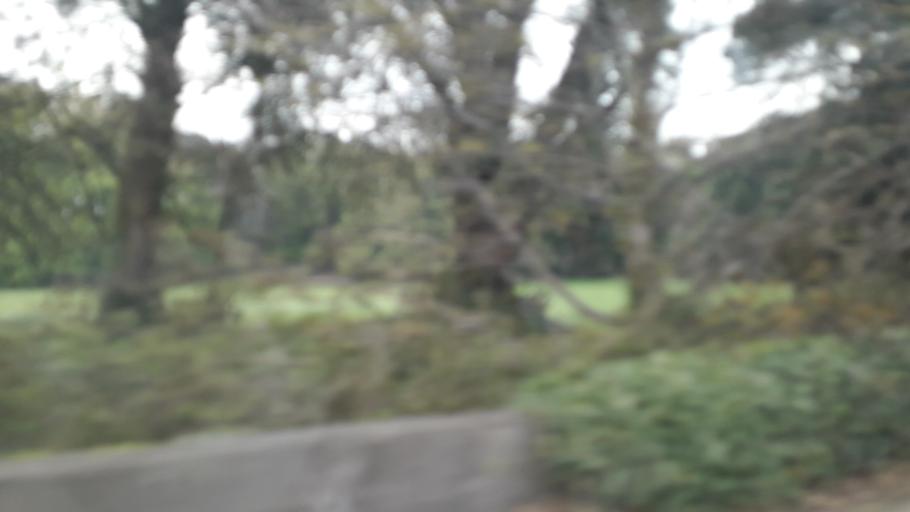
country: IE
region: Leinster
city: Dollymount
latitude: 53.3699
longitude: -6.1686
